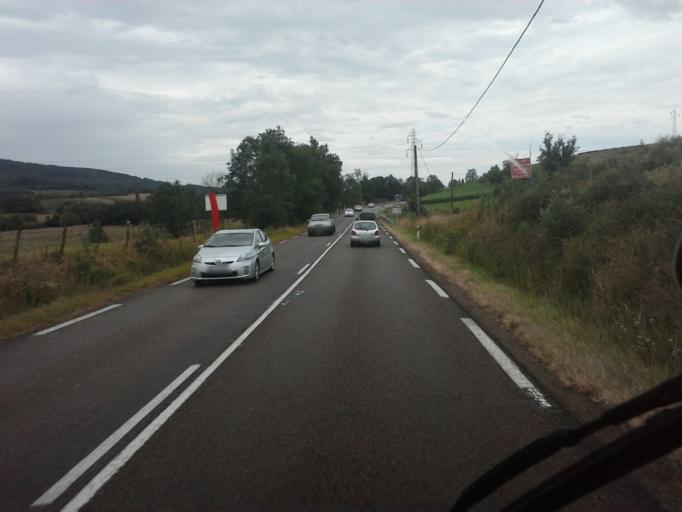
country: FR
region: Franche-Comte
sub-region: Departement du Jura
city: Arbois
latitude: 46.8885
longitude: 5.7292
